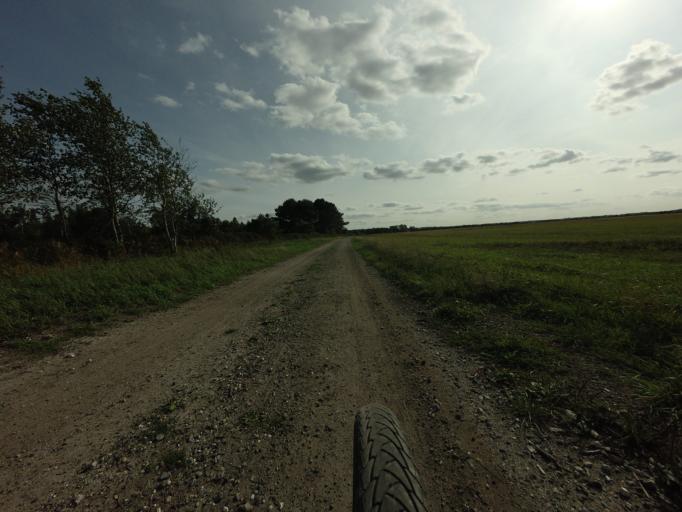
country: DK
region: Zealand
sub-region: Vordingborg Kommune
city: Praesto
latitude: 55.1479
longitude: 12.0920
